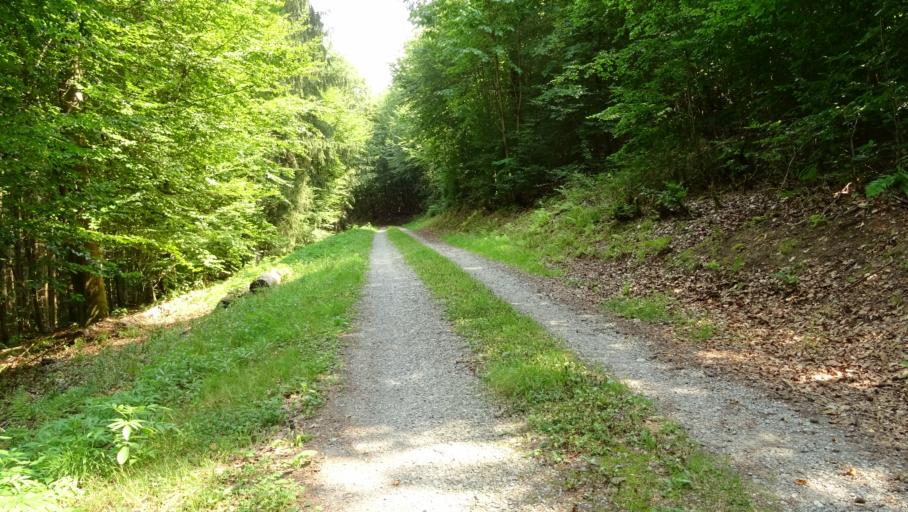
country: DE
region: Baden-Wuerttemberg
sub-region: Karlsruhe Region
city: Neckargerach
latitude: 49.4014
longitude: 9.0824
